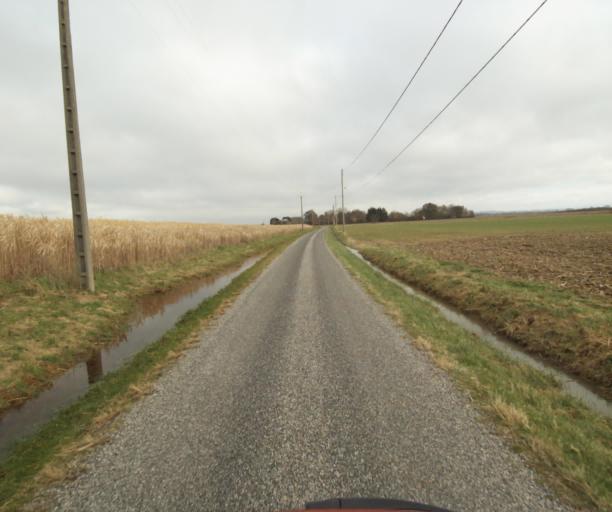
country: FR
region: Midi-Pyrenees
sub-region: Departement de l'Ariege
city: Mazeres
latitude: 43.1848
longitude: 1.6631
